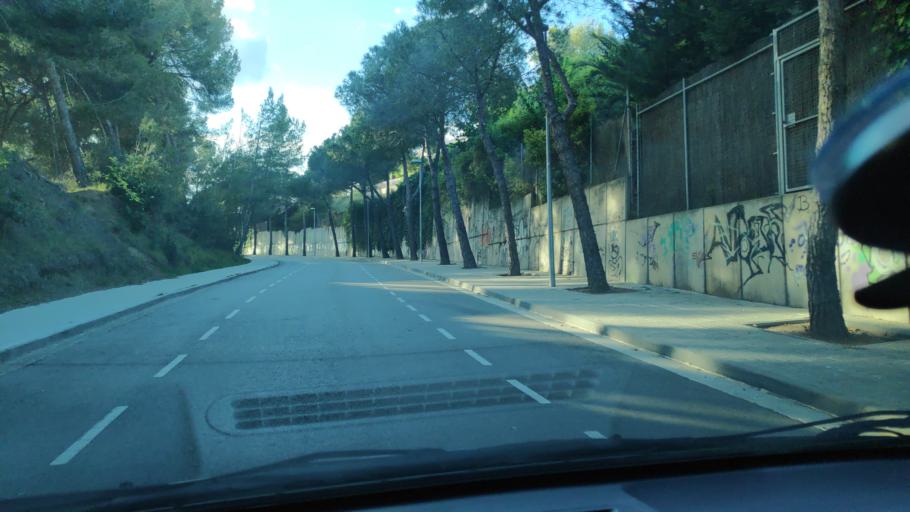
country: ES
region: Catalonia
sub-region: Provincia de Barcelona
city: Sant Quirze del Valles
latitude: 41.5382
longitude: 2.0717
